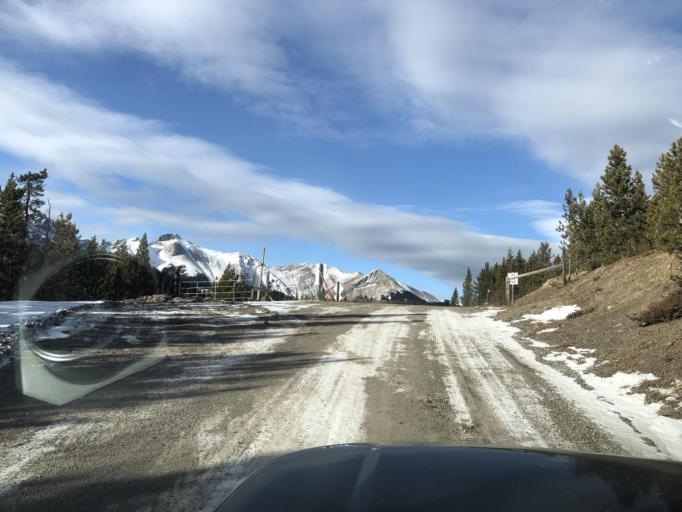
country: CA
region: Alberta
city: Canmore
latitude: 50.9402
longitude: -114.9387
